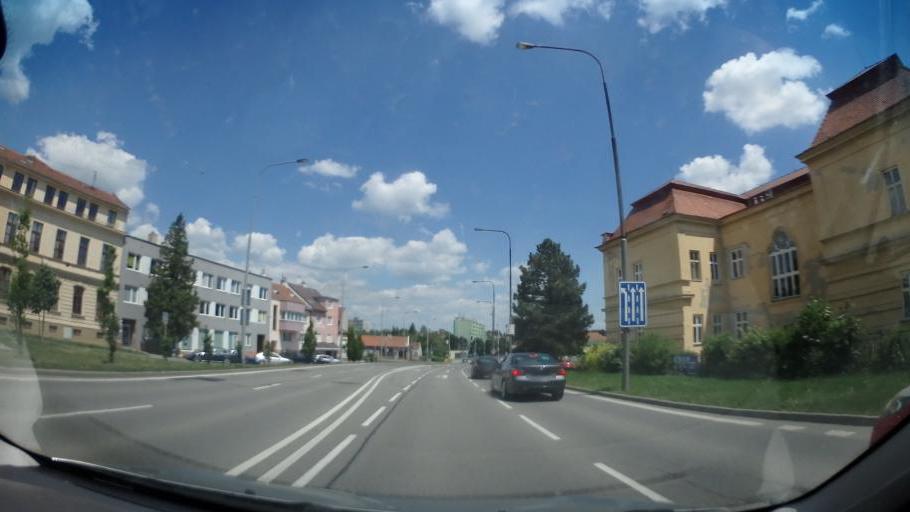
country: CZ
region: South Moravian
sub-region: Okres Vyskov
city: Vyskov
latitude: 49.2785
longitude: 16.9972
